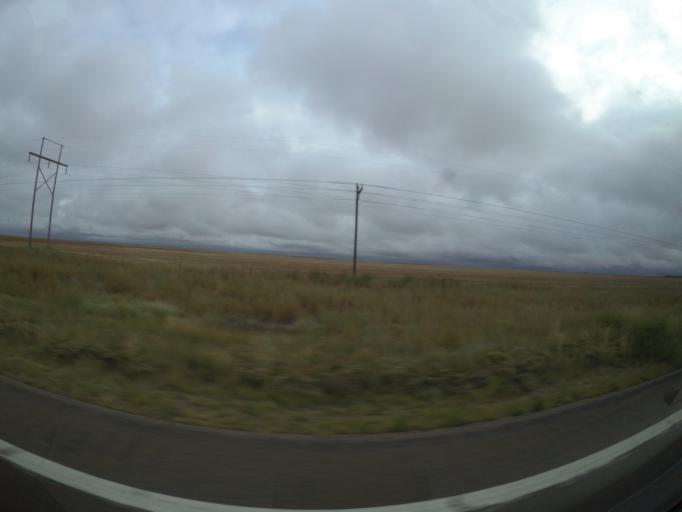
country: US
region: Colorado
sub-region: Washington County
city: Akron
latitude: 39.7404
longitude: -103.2662
